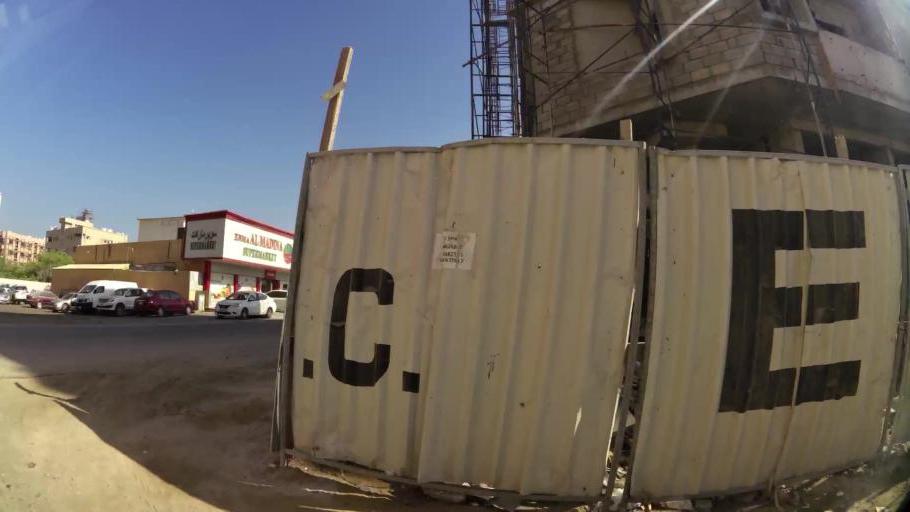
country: AE
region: Ajman
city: Ajman
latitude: 25.4195
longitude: 55.4508
